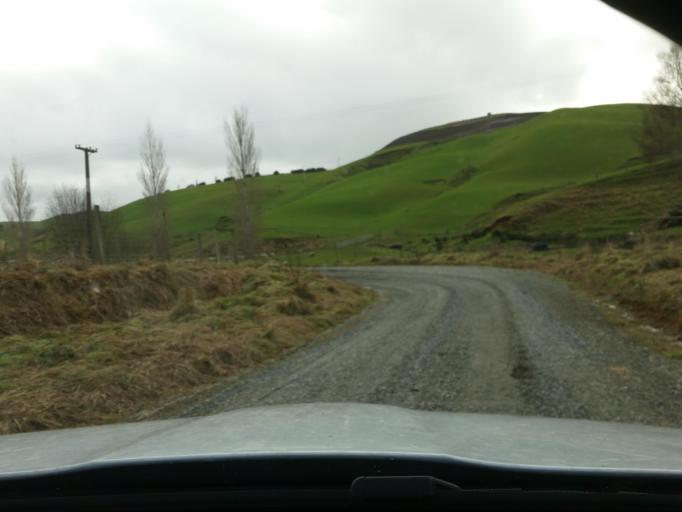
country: NZ
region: Southland
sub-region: Southland District
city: Riverton
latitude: -46.0646
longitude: 167.7831
